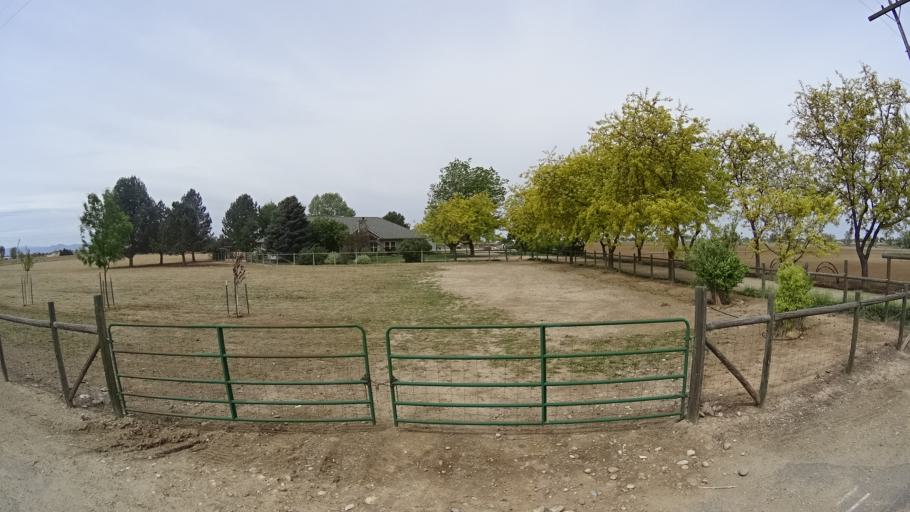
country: US
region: Idaho
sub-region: Ada County
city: Kuna
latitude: 43.5541
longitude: -116.4737
